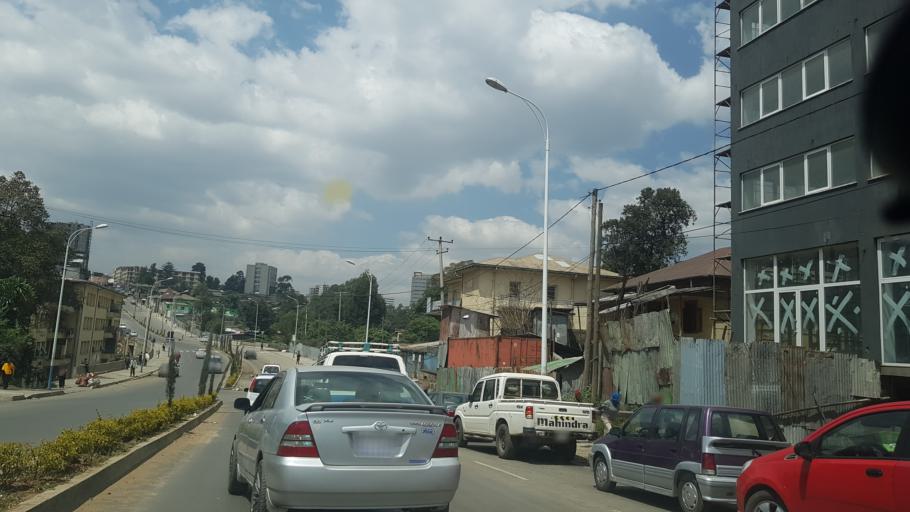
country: ET
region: Adis Abeba
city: Addis Ababa
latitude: 9.0275
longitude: 38.7507
